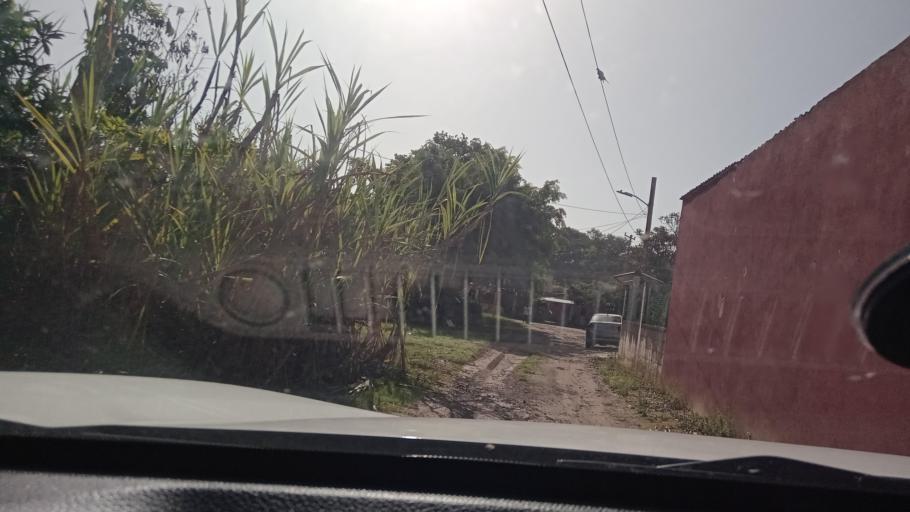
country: MX
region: Veracruz
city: El Castillo
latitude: 19.5662
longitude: -96.8645
